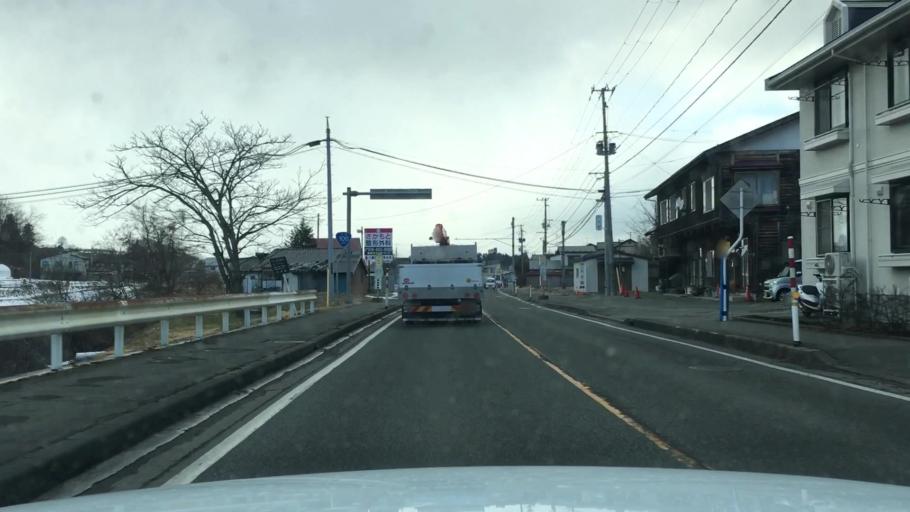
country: JP
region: Iwate
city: Morioka-shi
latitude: 39.6880
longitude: 141.1791
